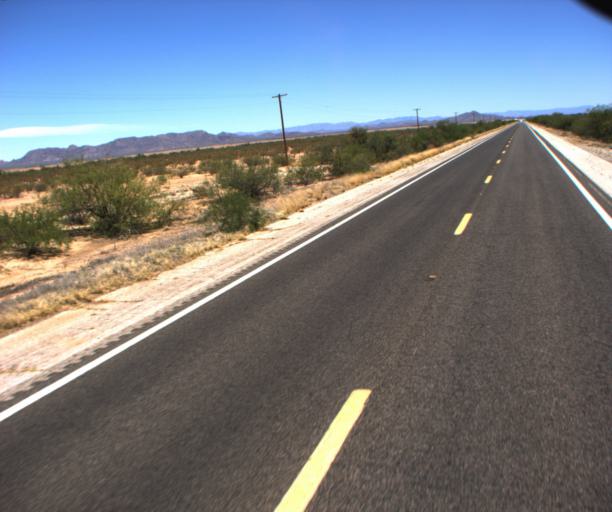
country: US
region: Arizona
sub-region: La Paz County
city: Salome
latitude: 33.9284
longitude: -113.2246
